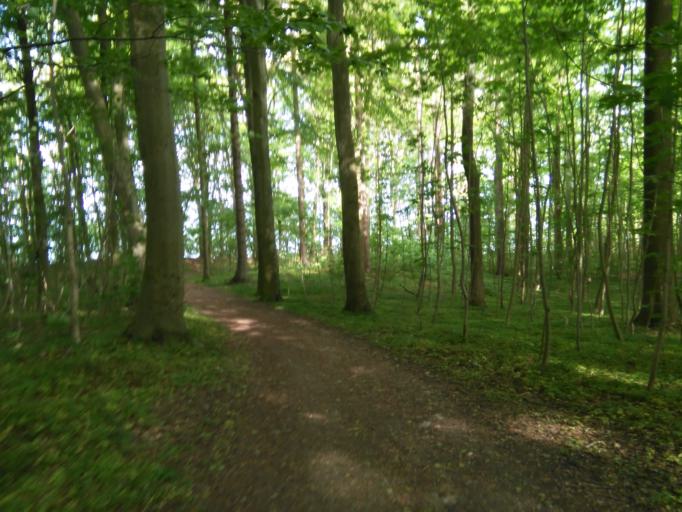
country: DK
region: Central Jutland
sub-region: Arhus Kommune
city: Beder
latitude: 56.0681
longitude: 10.2556
